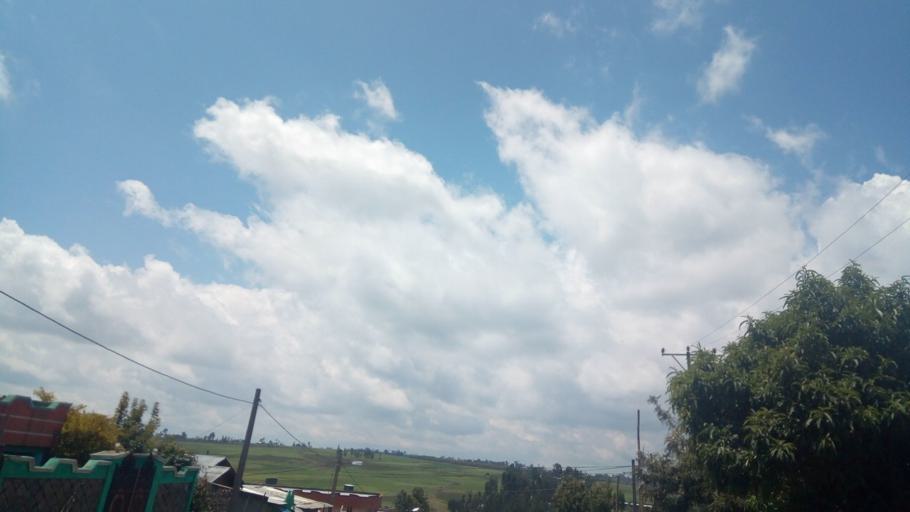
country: ET
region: Oromiya
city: Sendafa
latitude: 8.9718
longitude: 39.1196
